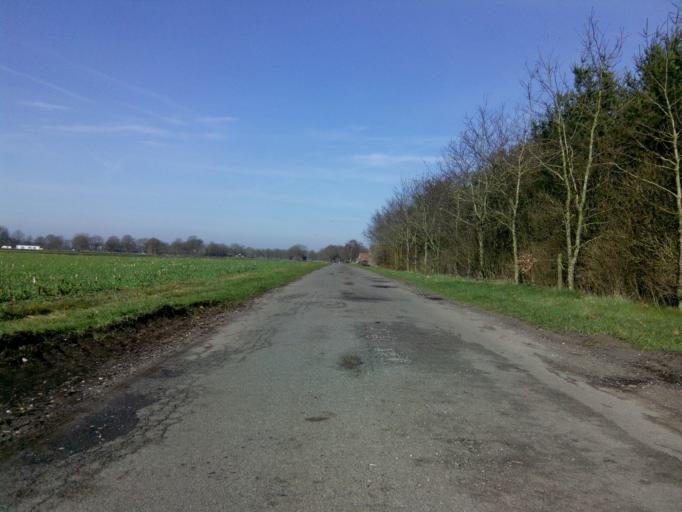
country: NL
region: Gelderland
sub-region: Gemeente Ede
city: Harskamp
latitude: 52.1518
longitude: 5.7257
